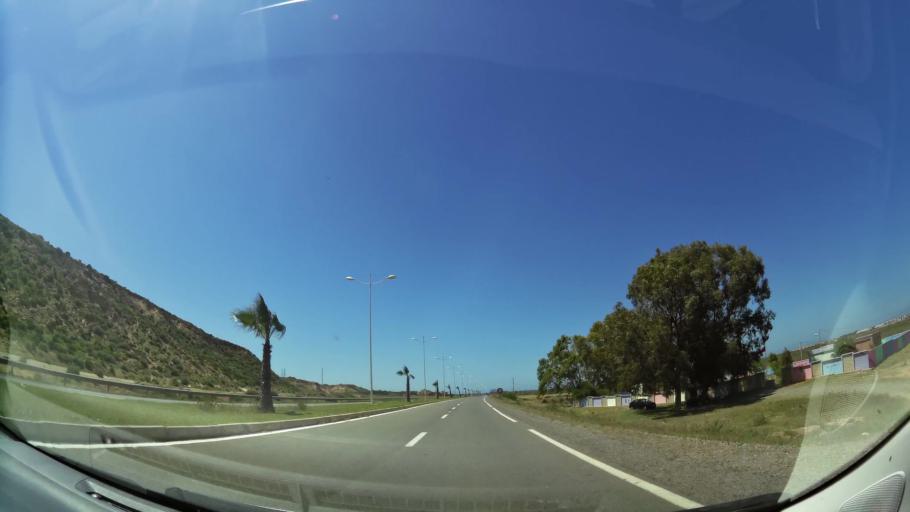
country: MA
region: Oriental
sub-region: Berkane-Taourirt
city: Madagh
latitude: 35.0948
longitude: -2.3165
